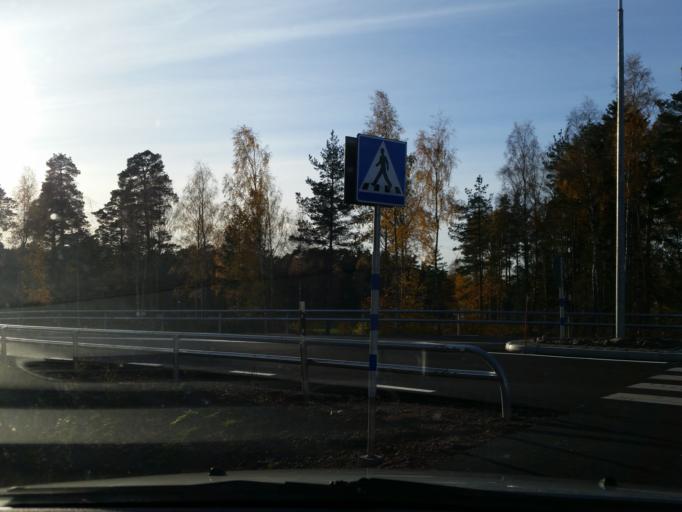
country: AX
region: Alands landsbygd
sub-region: Jomala
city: Jomala
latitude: 60.1121
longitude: 19.9805
